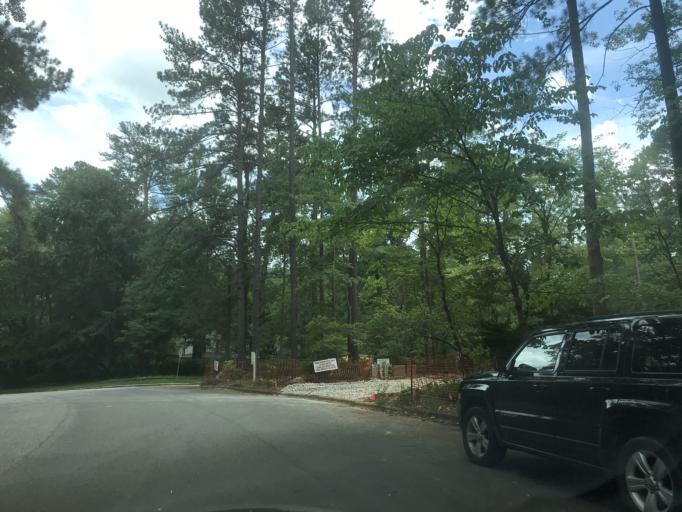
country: US
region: North Carolina
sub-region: Wake County
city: West Raleigh
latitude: 35.8297
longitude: -78.6536
